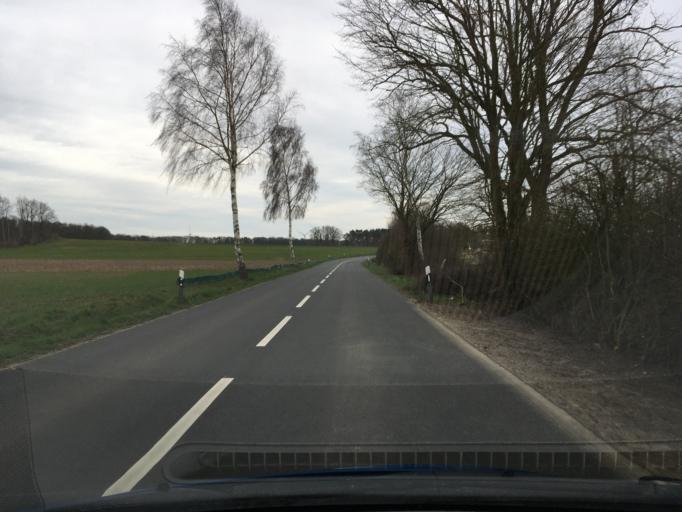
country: DE
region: Lower Saxony
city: Emmendorf
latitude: 53.0397
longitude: 10.6044
